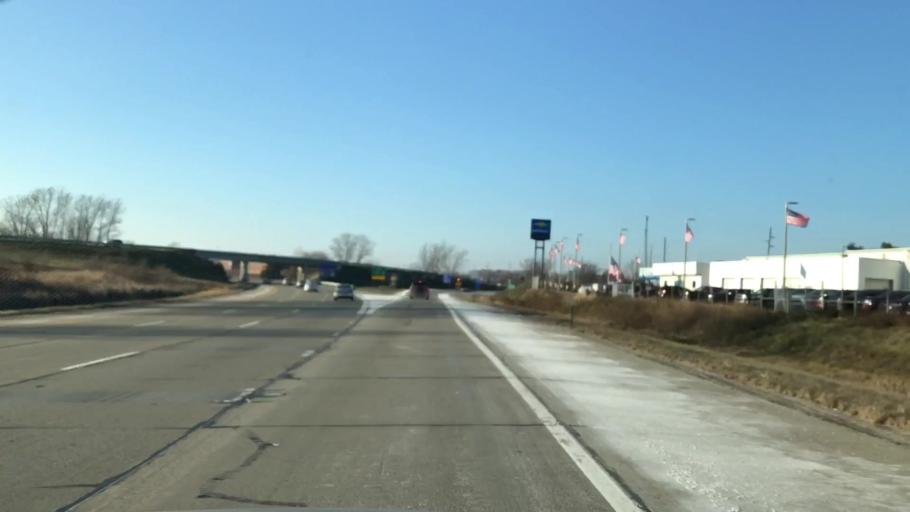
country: US
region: Michigan
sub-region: Livingston County
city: Howell
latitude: 42.5781
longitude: -83.8538
